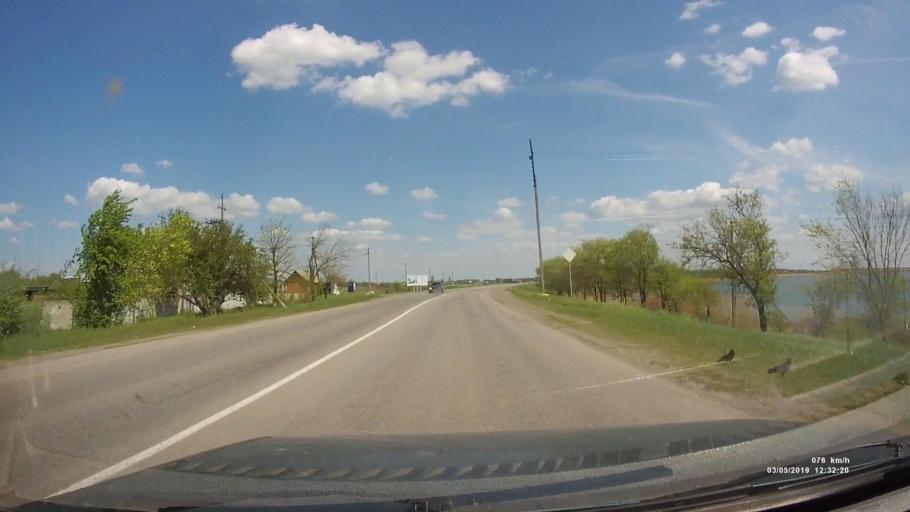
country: RU
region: Rostov
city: Semikarakorsk
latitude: 47.5111
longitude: 40.7580
